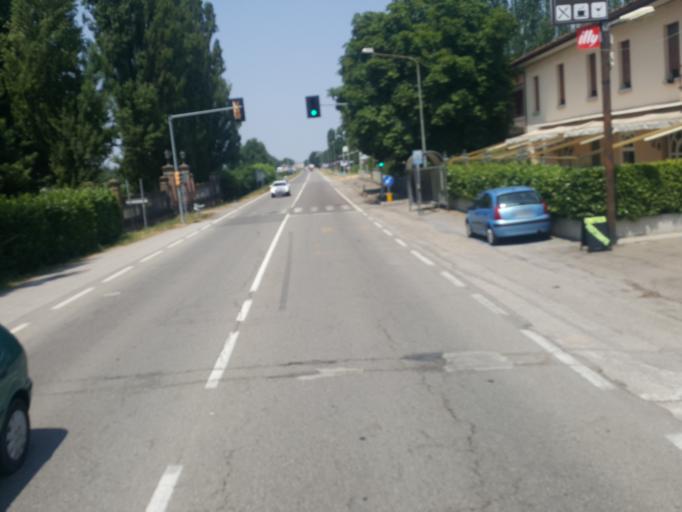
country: IT
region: Emilia-Romagna
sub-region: Provincia di Bologna
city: Calcara
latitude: 44.5634
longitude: 11.1429
